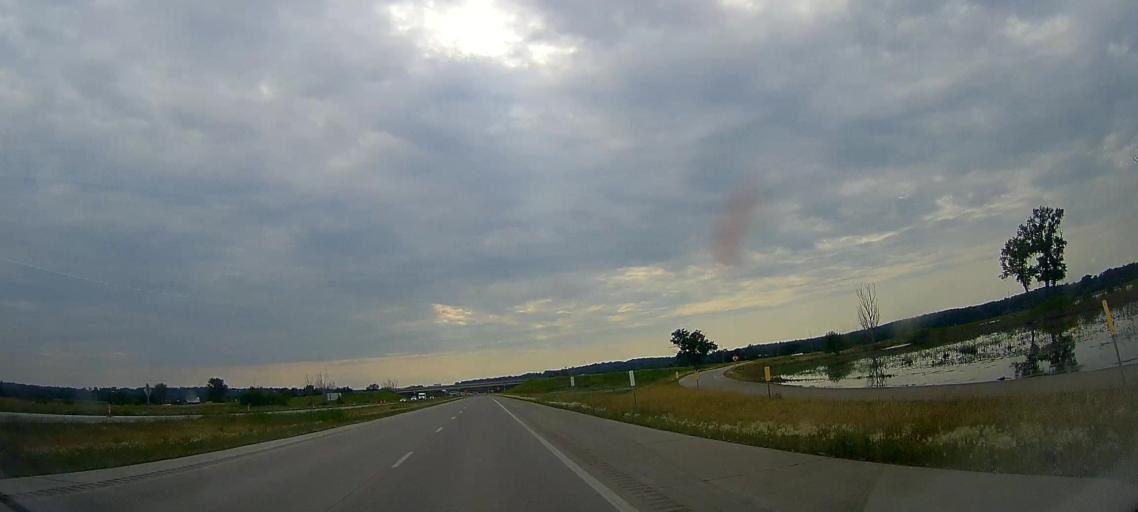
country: US
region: Iowa
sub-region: Pottawattamie County
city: Carter Lake
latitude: 41.3466
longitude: -95.9312
